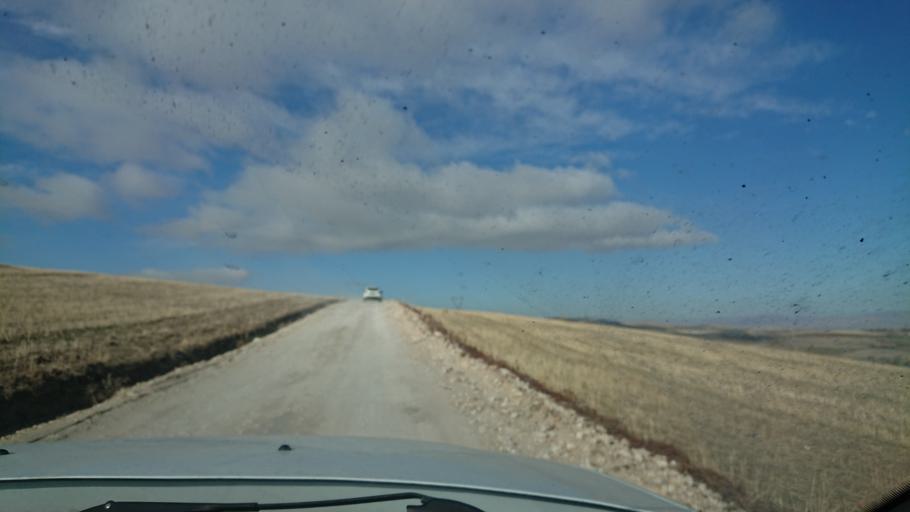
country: TR
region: Aksaray
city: Agacoren
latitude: 38.8488
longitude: 33.9480
